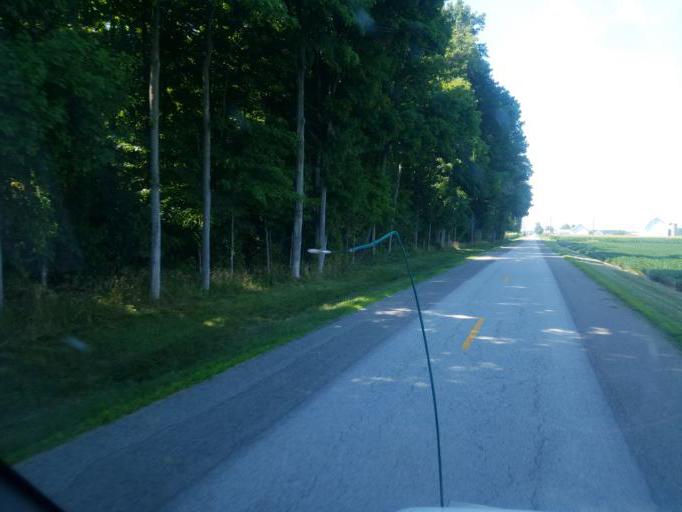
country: US
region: Ohio
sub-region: Shelby County
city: Jackson Center
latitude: 40.5250
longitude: -84.0119
